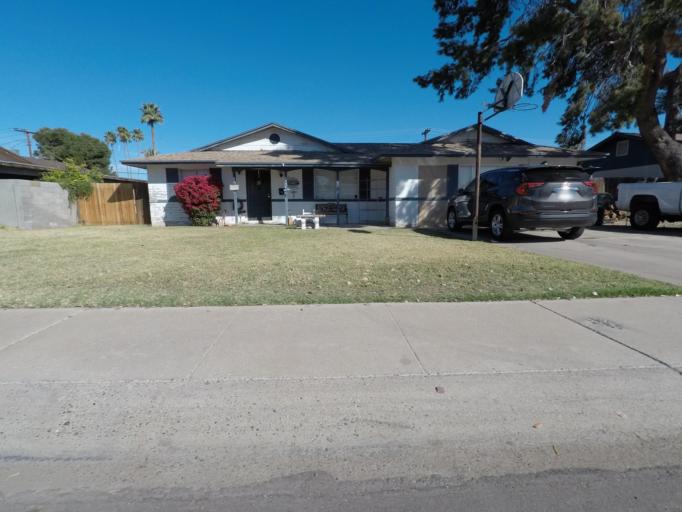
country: US
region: Arizona
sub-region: Maricopa County
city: Glendale
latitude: 33.5467
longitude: -112.1405
